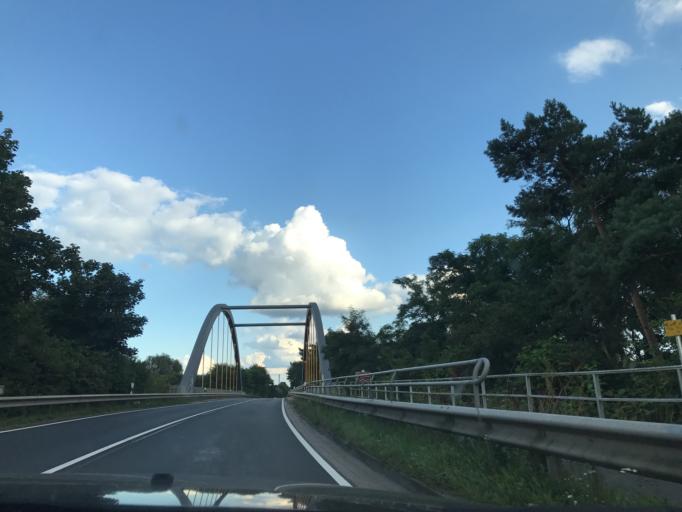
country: DE
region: Lower Saxony
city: Klein Schwulper
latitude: 52.3120
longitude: 10.4572
